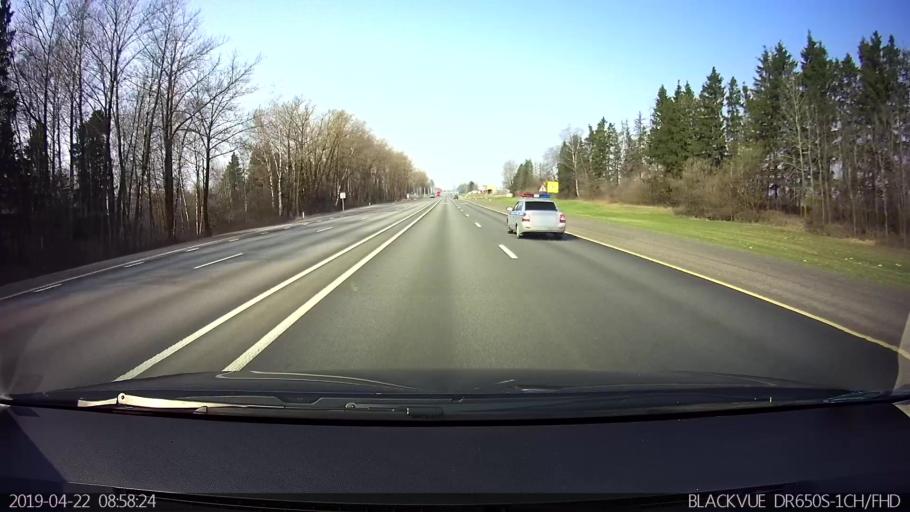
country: RU
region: Smolensk
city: Pechersk
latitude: 54.8651
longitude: 31.9934
